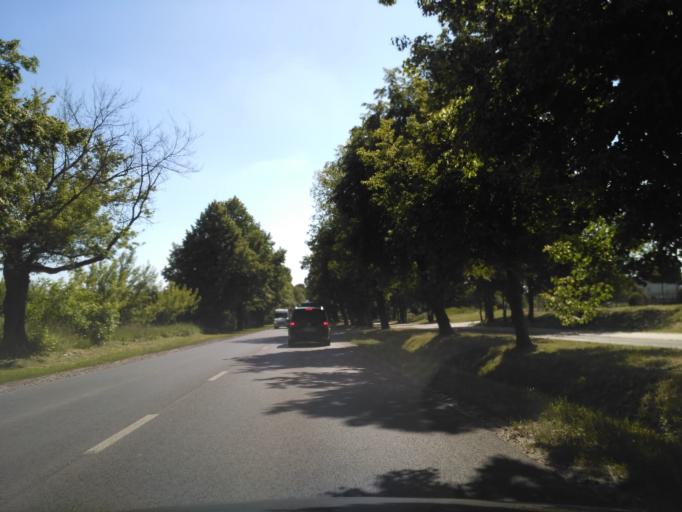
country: PL
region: Lublin Voivodeship
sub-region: Powiat lubelski
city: Lublin
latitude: 51.2009
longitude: 22.5567
